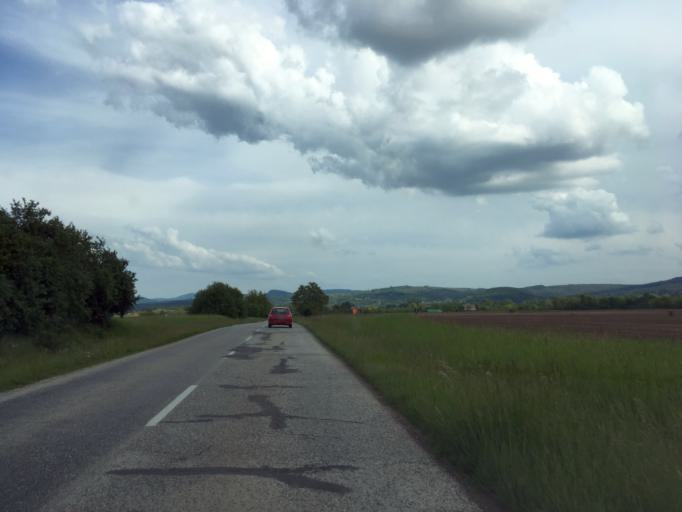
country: HU
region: Komarom-Esztergom
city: Dunaalmas
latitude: 47.7507
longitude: 18.3268
